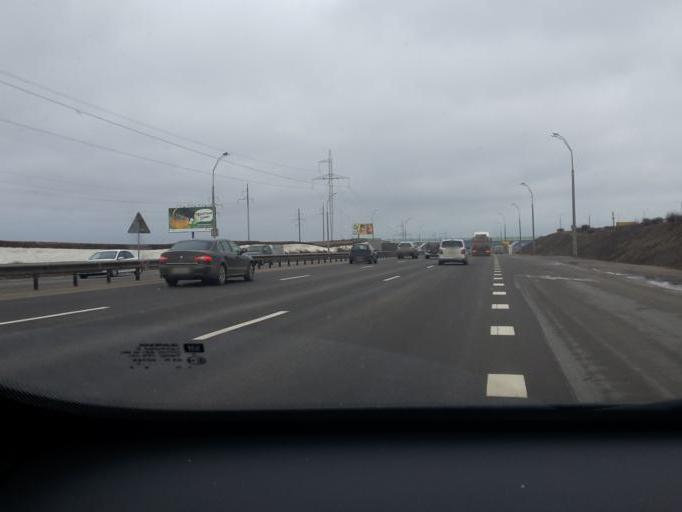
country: BY
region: Minsk
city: Malinovka
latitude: 53.8823
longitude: 27.4167
